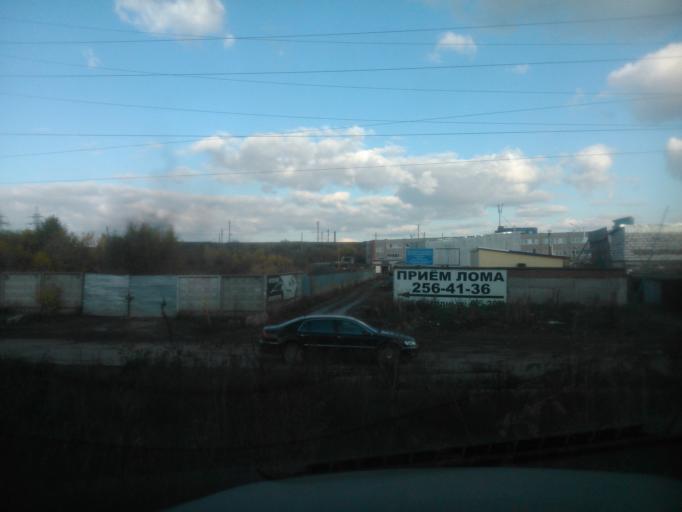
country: RU
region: Perm
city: Kondratovo
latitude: 58.0060
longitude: 56.1509
